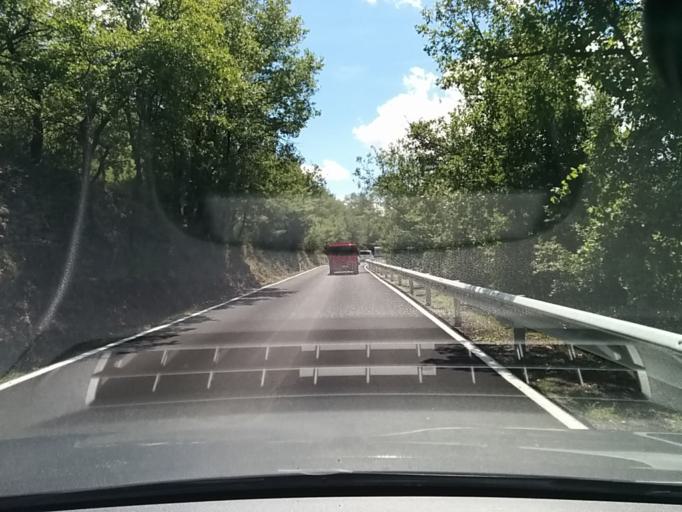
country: ES
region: Aragon
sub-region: Provincia de Huesca
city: Fiscal
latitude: 42.4953
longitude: -0.1077
